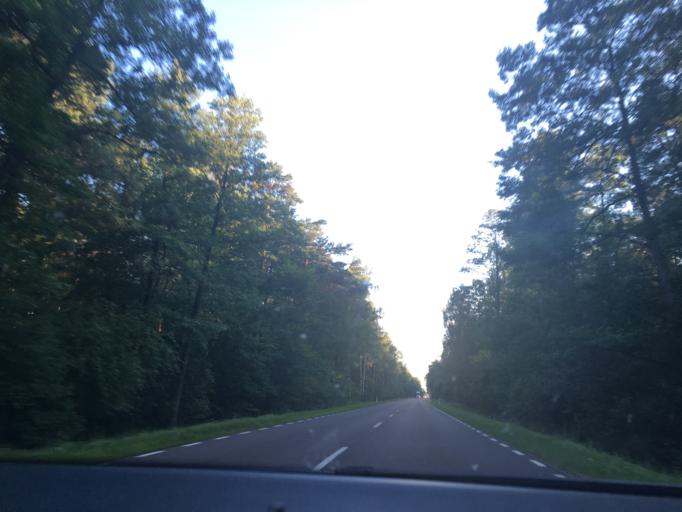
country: PL
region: Lublin Voivodeship
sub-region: Powiat bialski
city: Rzeczyca
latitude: 51.9471
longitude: 22.7294
